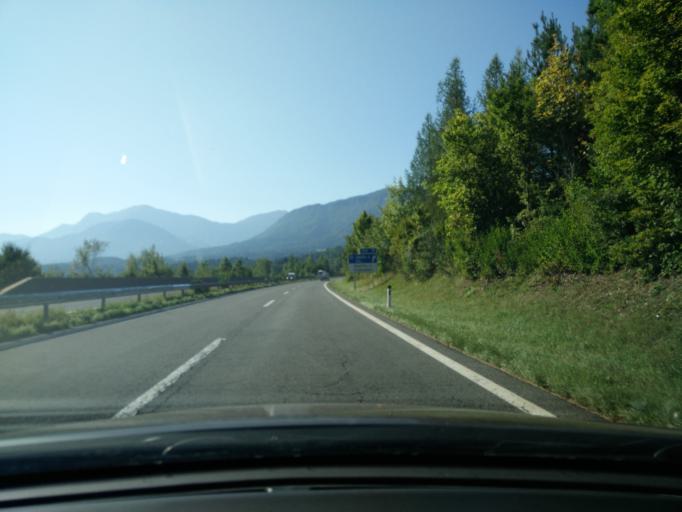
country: AT
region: Carinthia
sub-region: Politischer Bezirk Villach Land
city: Rosegg
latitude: 46.5687
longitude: 14.0063
